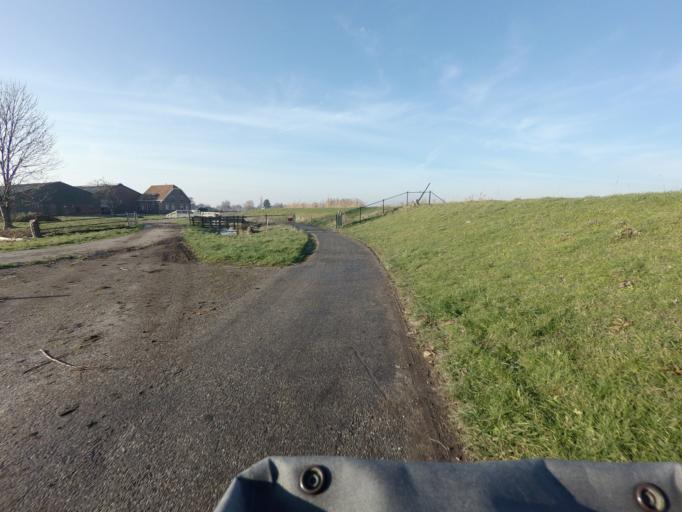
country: NL
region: Utrecht
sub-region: Gemeente De Ronde Venen
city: Mijdrecht
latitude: 52.1792
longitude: 4.8500
